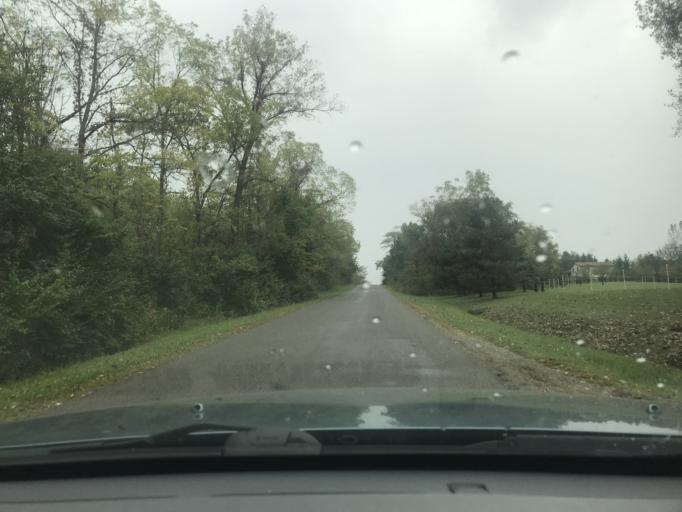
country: US
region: Ohio
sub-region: Champaign County
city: North Lewisburg
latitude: 40.1816
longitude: -83.6408
